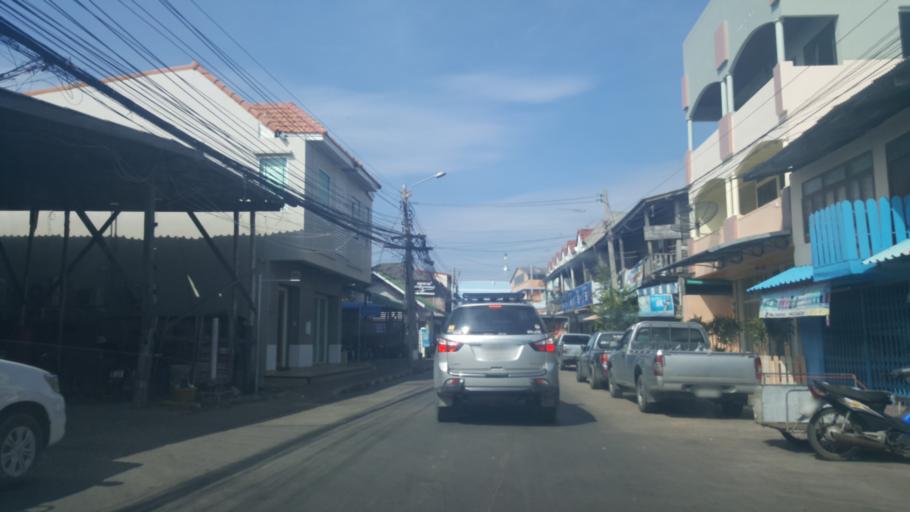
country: TH
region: Chon Buri
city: Sattahip
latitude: 12.6629
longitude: 100.9025
